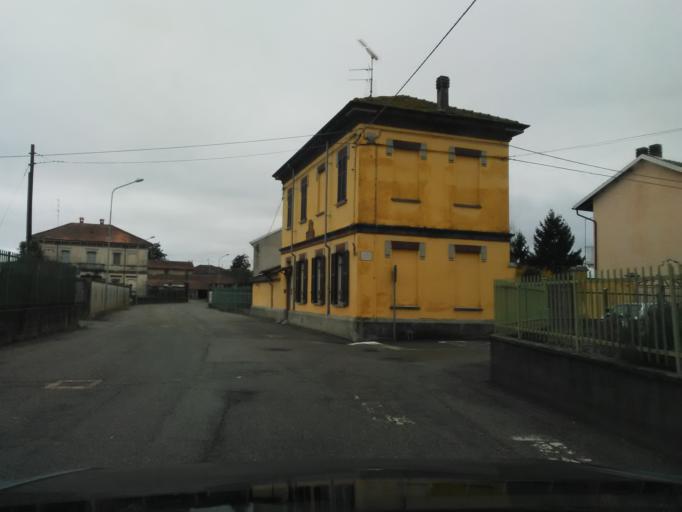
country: IT
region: Piedmont
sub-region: Provincia di Vercelli
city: Olcenengo
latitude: 45.3609
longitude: 8.3098
